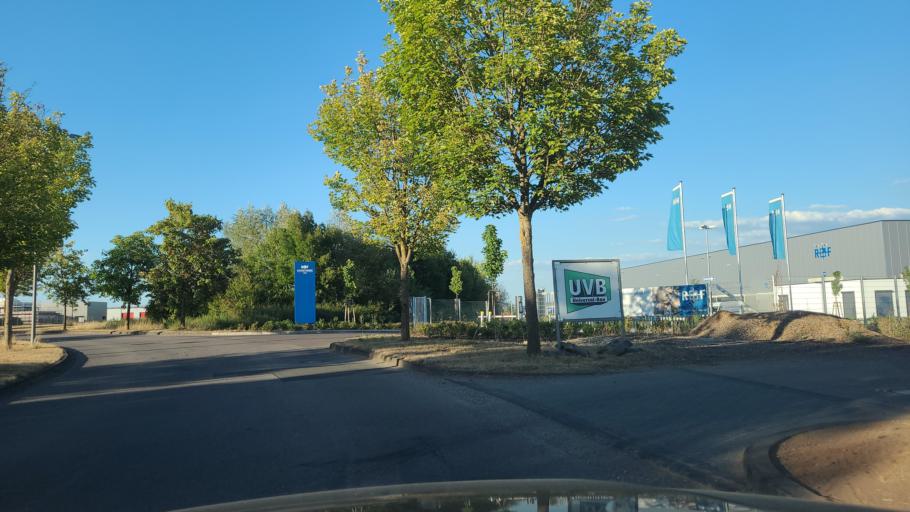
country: DE
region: Rheinland-Pfalz
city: Bekond
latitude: 49.8610
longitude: 6.7972
